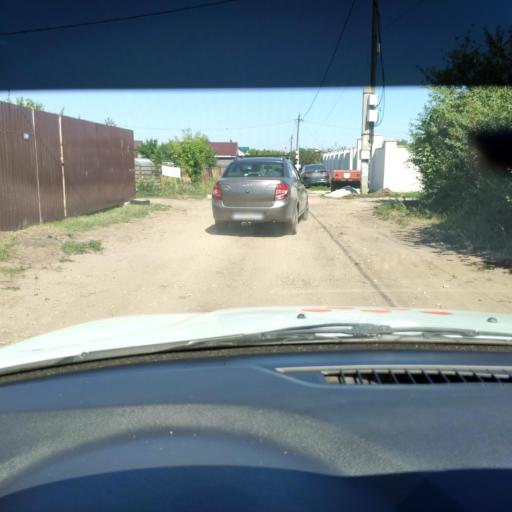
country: RU
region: Samara
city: Tol'yatti
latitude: 53.5695
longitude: 49.3704
